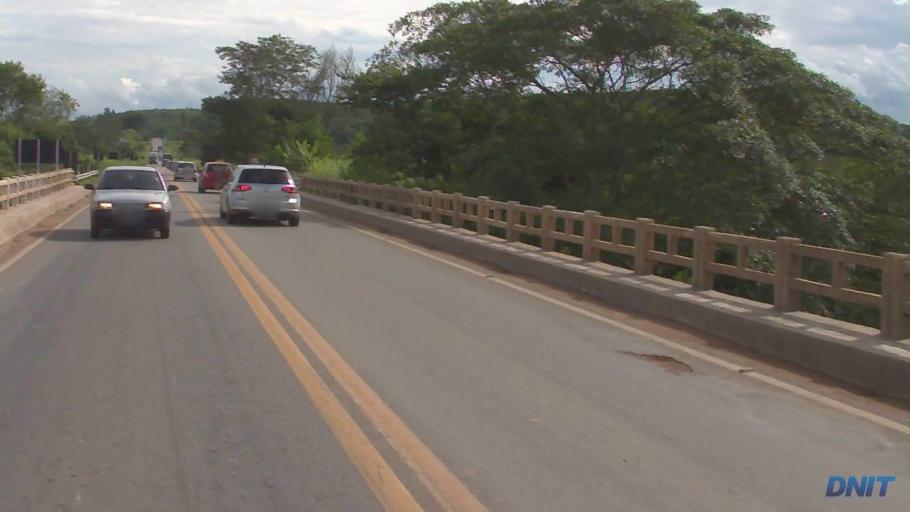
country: BR
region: Minas Gerais
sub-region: Belo Oriente
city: Belo Oriente
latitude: -19.2375
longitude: -42.3321
